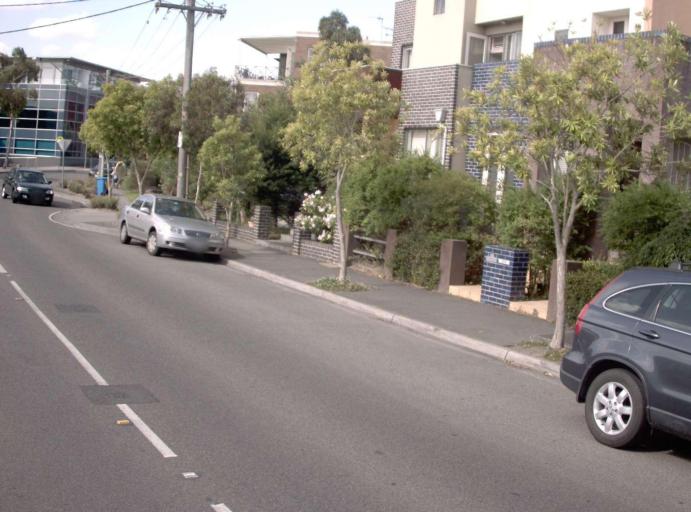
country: AU
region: Victoria
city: Glenferrie
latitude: -37.8301
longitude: 145.0529
